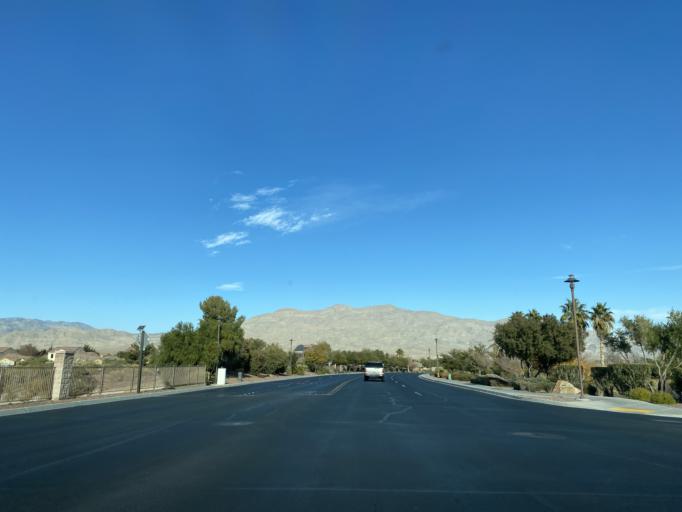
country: US
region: Nevada
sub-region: Clark County
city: North Las Vegas
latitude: 36.3140
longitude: -115.2585
